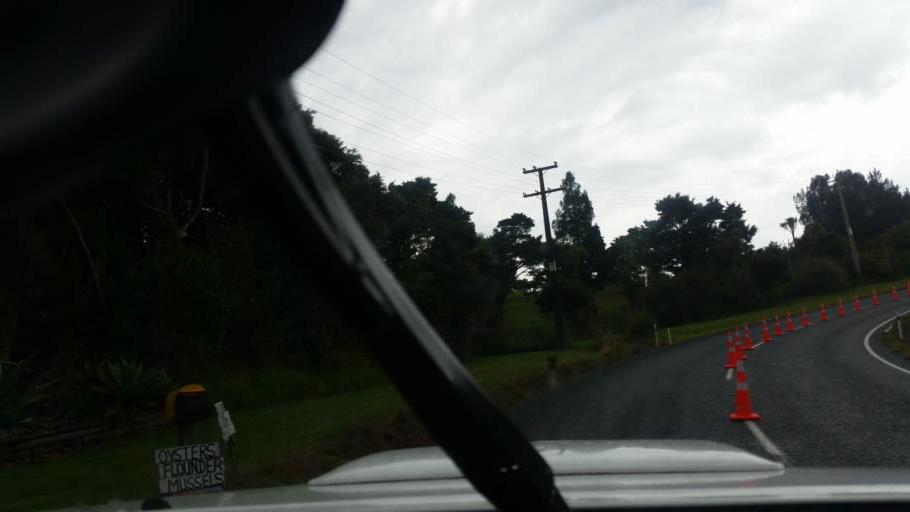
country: NZ
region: Auckland
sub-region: Auckland
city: Wellsford
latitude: -36.1493
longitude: 174.2205
